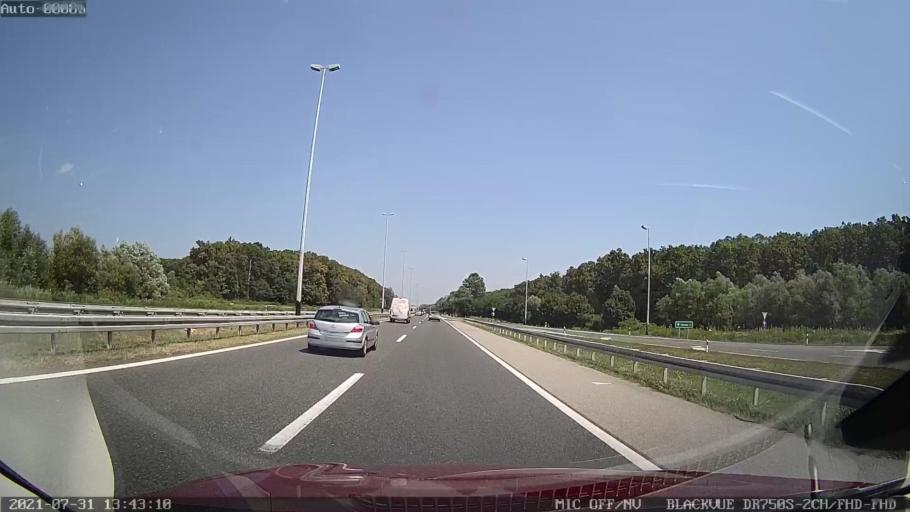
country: HR
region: Brodsko-Posavska
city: Oriovac
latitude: 45.1562
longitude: 17.8225
